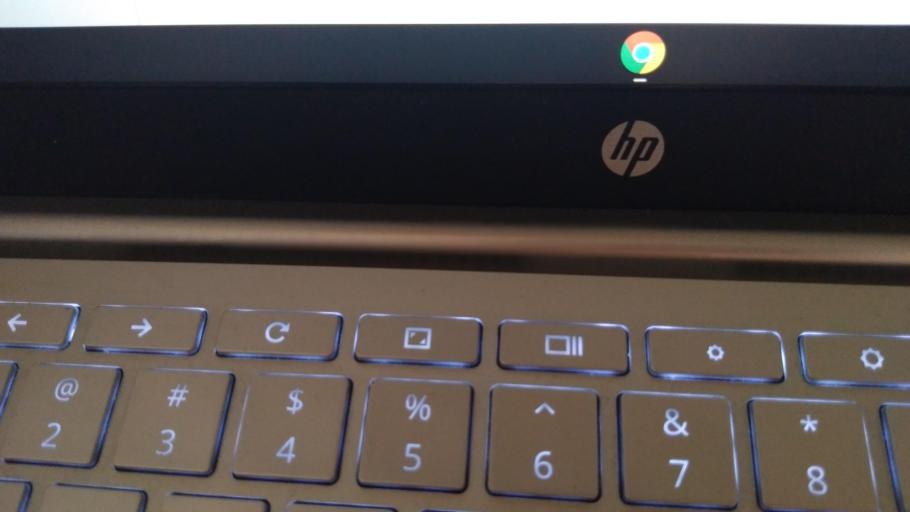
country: PH
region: Metro Manila
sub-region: Caloocan City
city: Niugan
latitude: 14.6790
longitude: 120.9659
